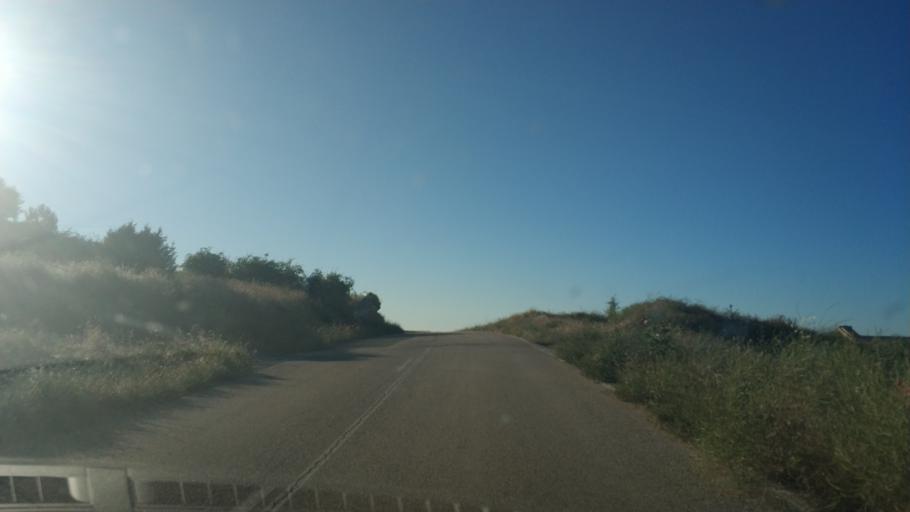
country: ES
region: Castille and Leon
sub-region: Provincia de Soria
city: Liceras
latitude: 41.4650
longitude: -3.2152
